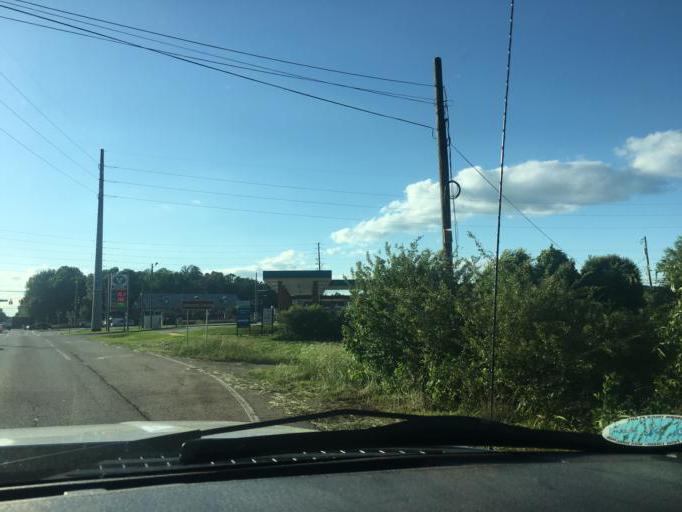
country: US
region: Georgia
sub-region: Forsyth County
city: Cumming
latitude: 34.2573
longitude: -84.0735
